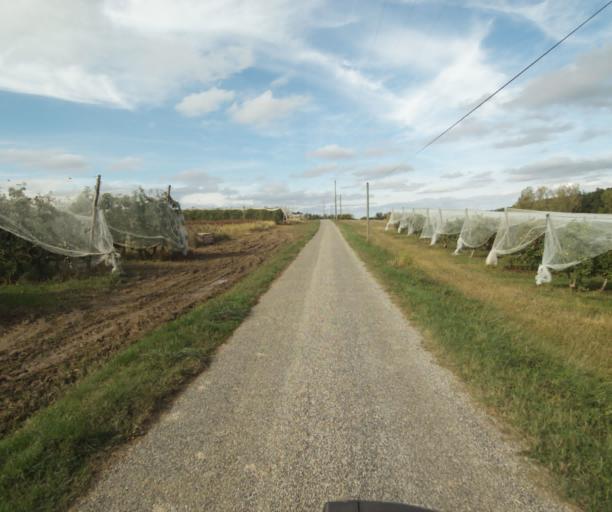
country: FR
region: Midi-Pyrenees
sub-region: Departement du Tarn-et-Garonne
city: Saint-Porquier
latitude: 43.9479
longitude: 1.1332
